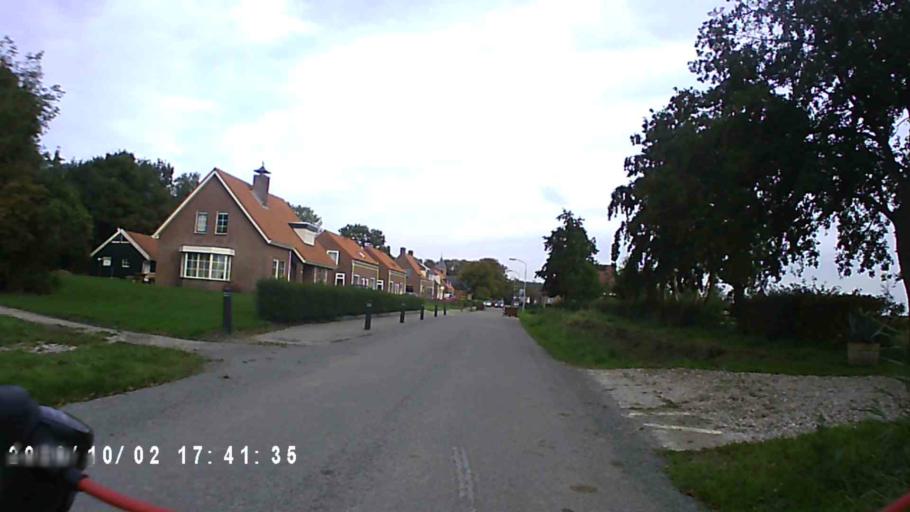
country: NL
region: Groningen
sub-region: Gemeente Zuidhorn
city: Oldehove
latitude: 53.3383
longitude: 6.3743
